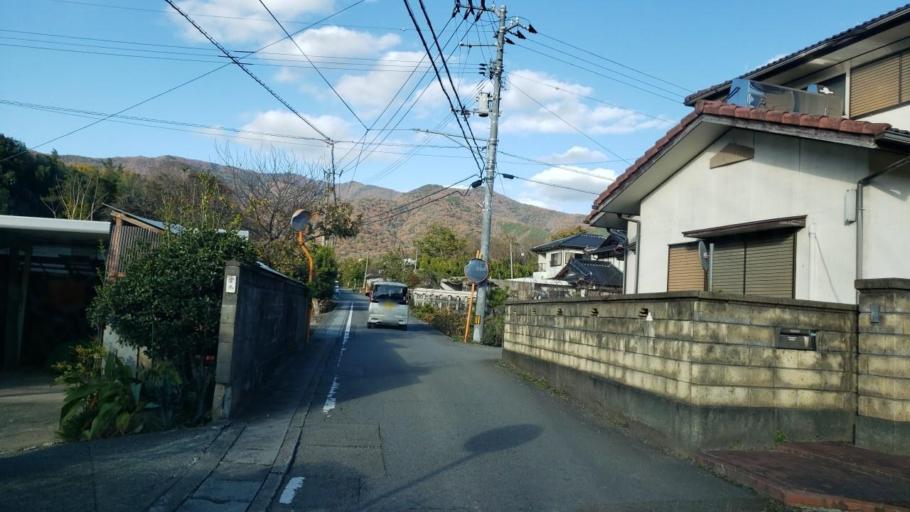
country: JP
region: Tokushima
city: Wakimachi
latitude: 34.0609
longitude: 134.0876
